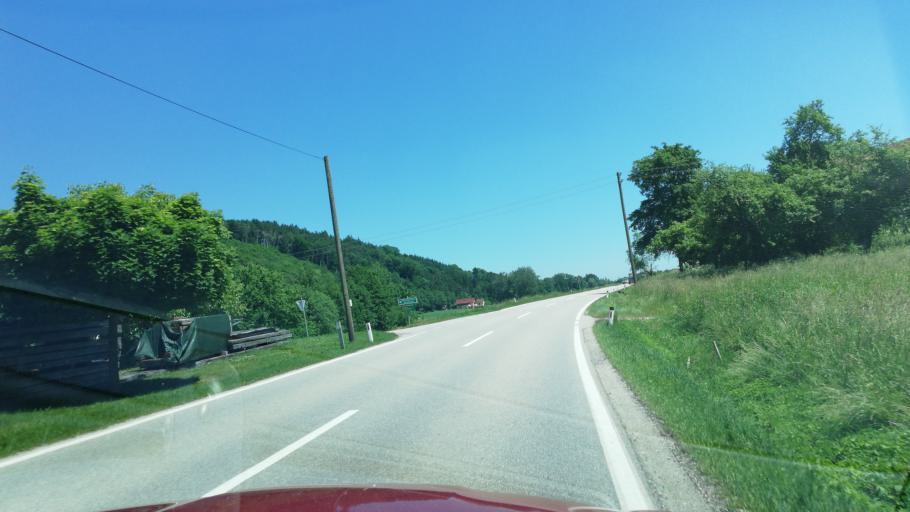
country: AT
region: Upper Austria
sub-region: Wels-Land
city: Offenhausen
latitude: 48.1576
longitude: 13.8511
